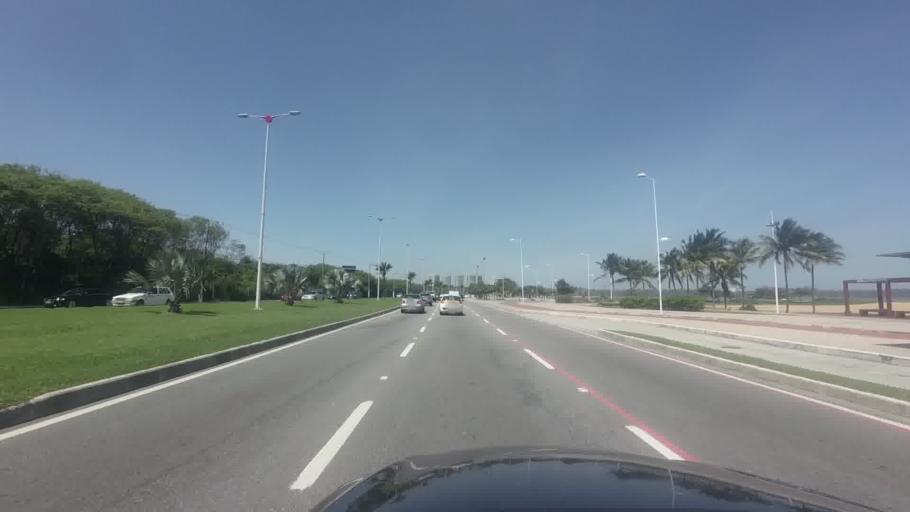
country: BR
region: Espirito Santo
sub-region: Vila Velha
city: Vila Velha
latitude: -20.2733
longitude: -40.2802
